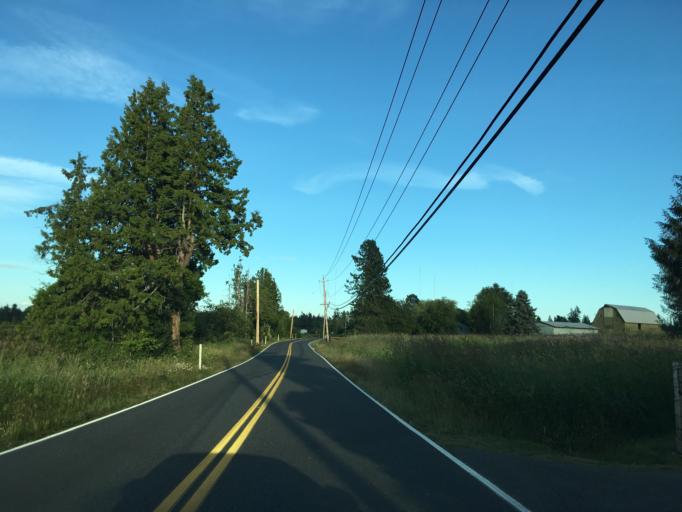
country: US
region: Washington
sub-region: Whatcom County
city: Blaine
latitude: 48.9599
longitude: -122.7546
